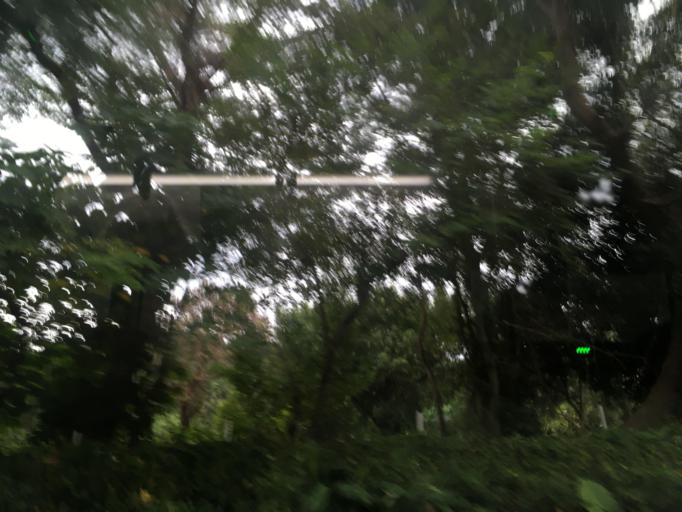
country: TW
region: Taipei
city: Taipei
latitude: 25.1351
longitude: 121.5288
